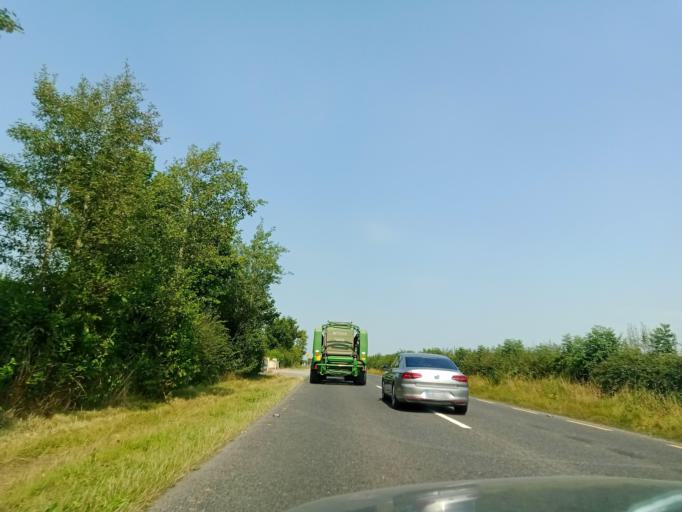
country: IE
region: Leinster
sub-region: Laois
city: Portlaoise
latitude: 53.0372
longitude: -7.2533
